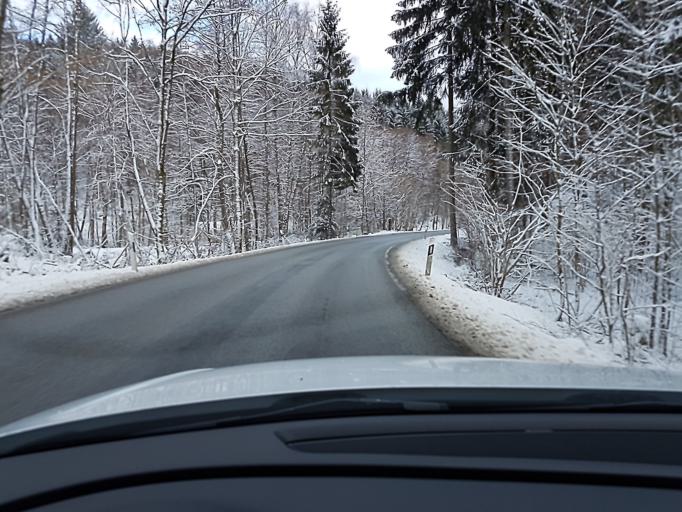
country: DE
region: Baden-Wuerttemberg
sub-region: Regierungsbezirk Stuttgart
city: Lowenstein
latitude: 49.0795
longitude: 9.4161
